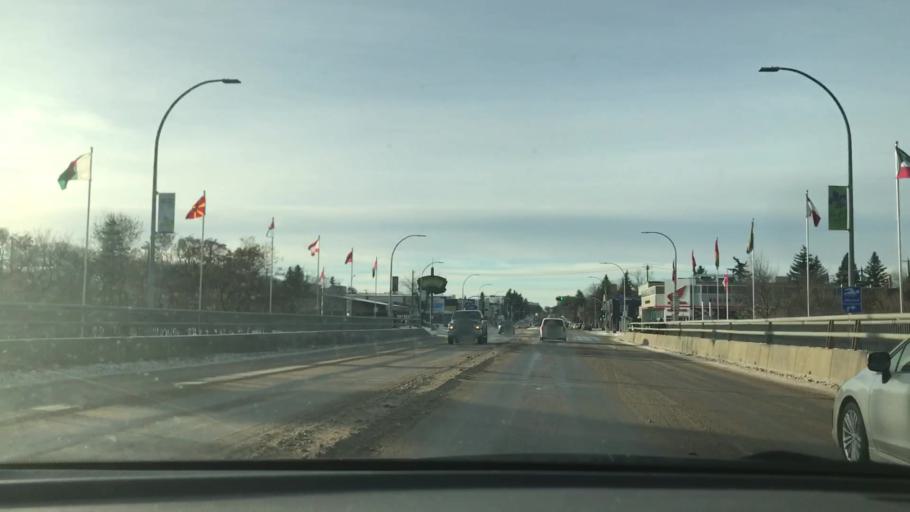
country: CA
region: Alberta
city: Edmonton
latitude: 53.5181
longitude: -113.4742
